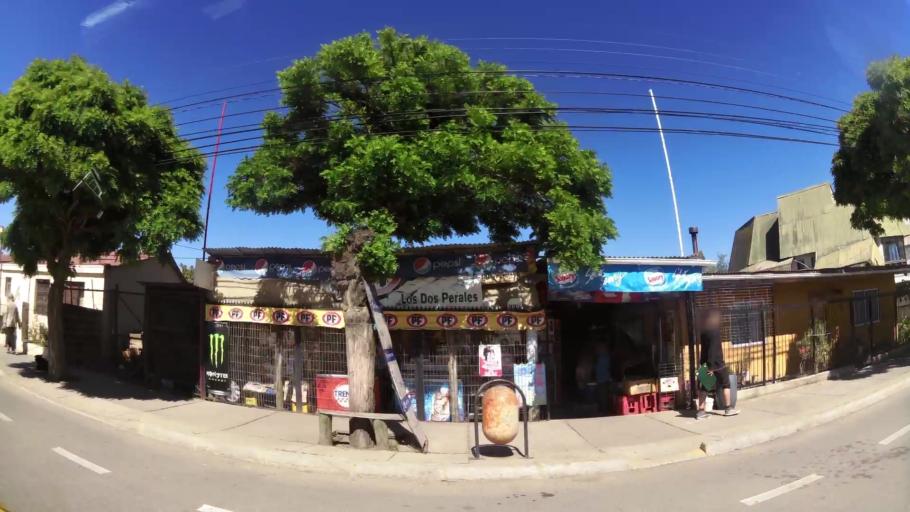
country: CL
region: Valparaiso
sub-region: Provincia de Marga Marga
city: Quilpue
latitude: -33.3159
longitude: -71.4090
